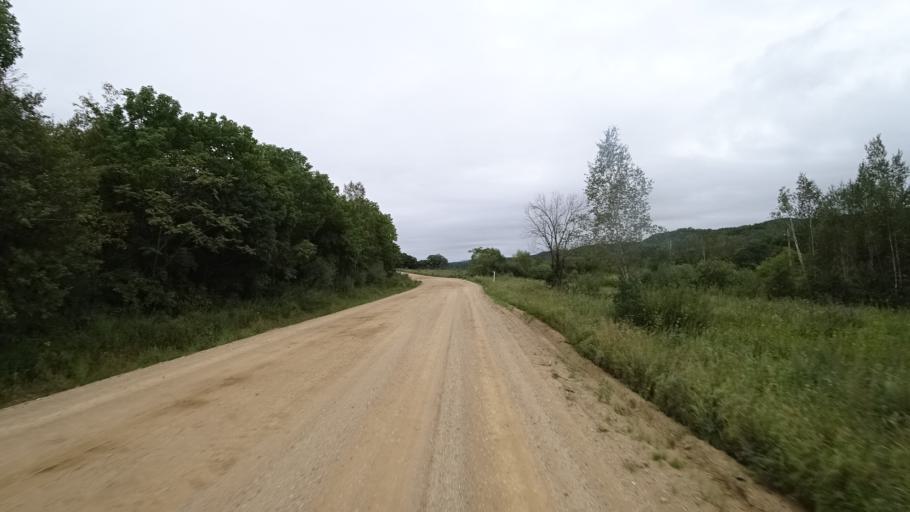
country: RU
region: Primorskiy
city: Rettikhovka
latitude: 44.1767
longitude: 132.8292
